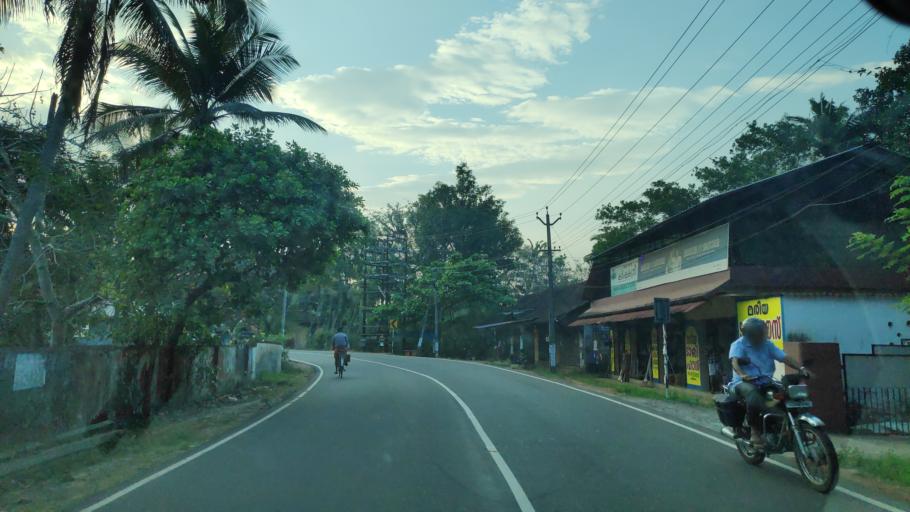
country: IN
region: Kerala
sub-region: Alappuzha
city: Shertallai
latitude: 9.6819
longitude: 76.3656
